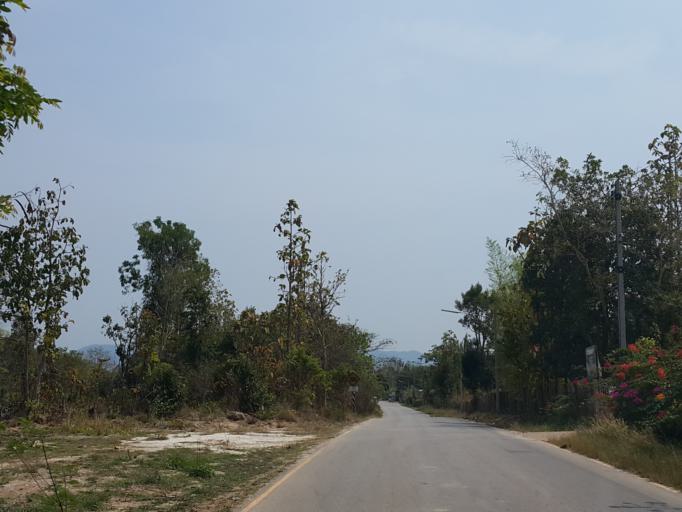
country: TH
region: Lampang
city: Lampang
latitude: 18.3056
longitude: 99.4244
